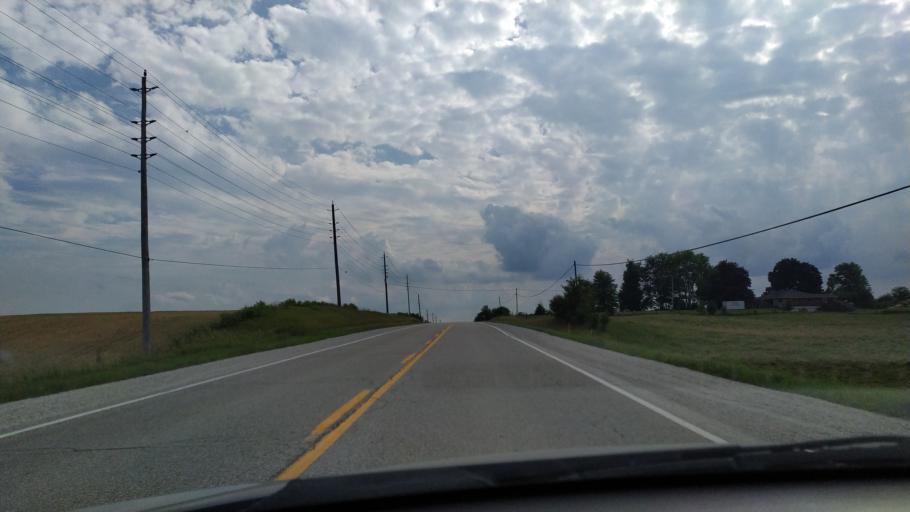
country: CA
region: Ontario
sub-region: Wellington County
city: Guelph
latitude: 43.4657
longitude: -80.1648
